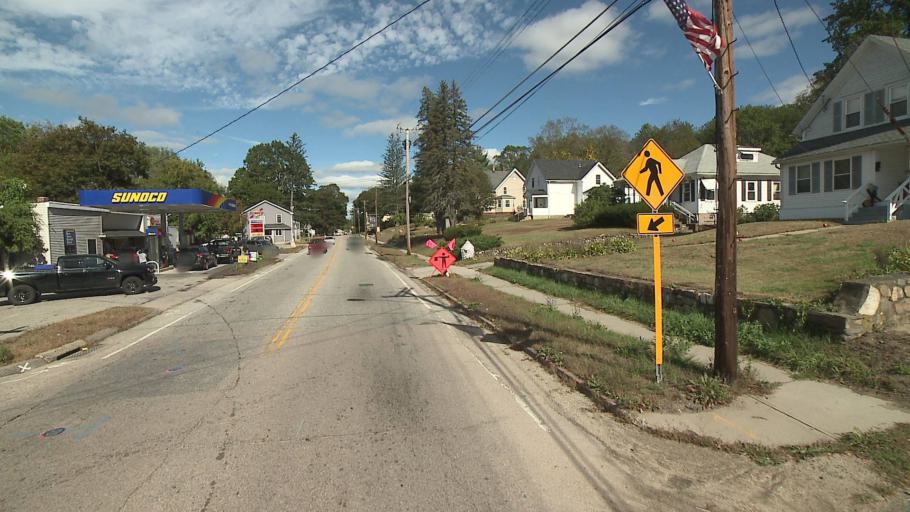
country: US
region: Connecticut
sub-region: Windham County
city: Danielson
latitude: 41.8159
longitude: -71.8769
